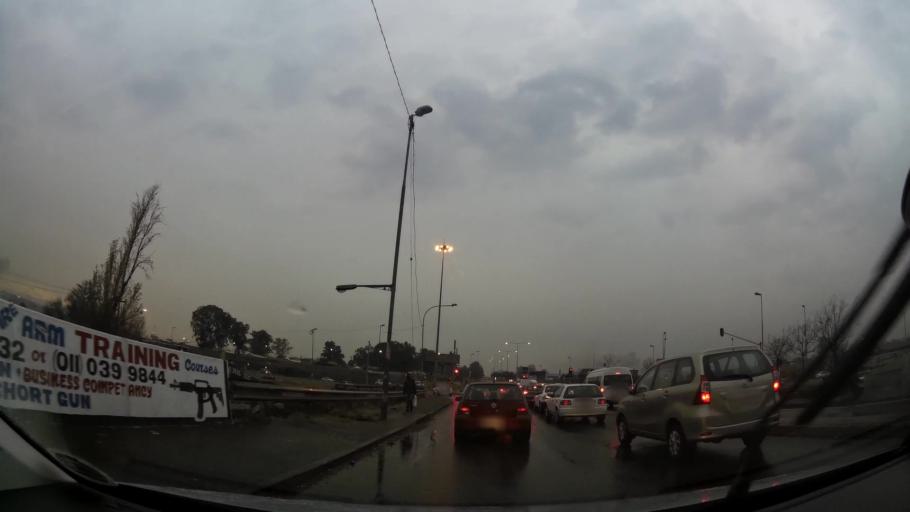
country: ZA
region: Gauteng
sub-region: City of Johannesburg Metropolitan Municipality
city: Soweto
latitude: -26.2625
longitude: 27.8894
